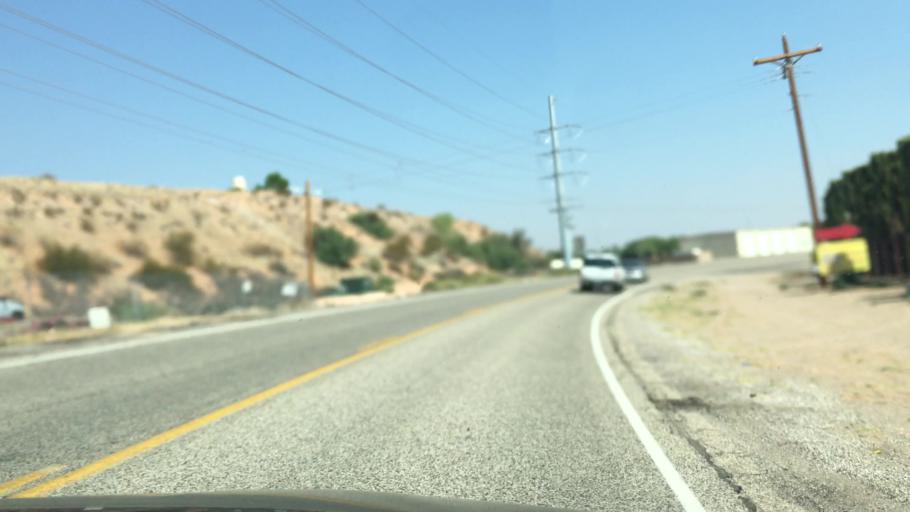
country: US
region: Arizona
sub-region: Mohave County
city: Beaver Dam
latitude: 36.8978
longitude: -113.9342
